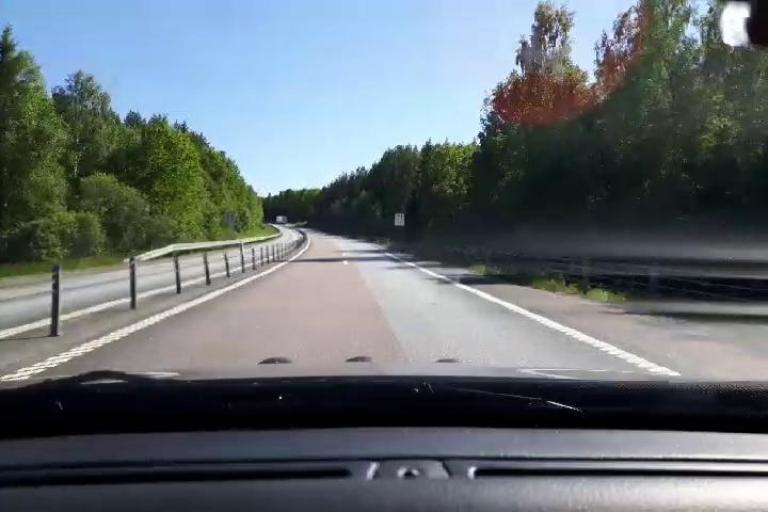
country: SE
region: Gaevleborg
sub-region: Soderhamns Kommun
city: Soderhamn
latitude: 61.2736
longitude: 17.0263
